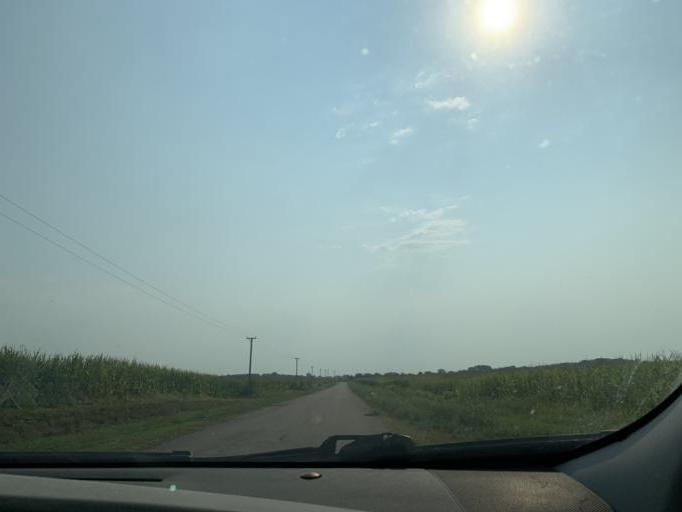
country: US
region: Illinois
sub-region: Whiteside County
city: Morrison
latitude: 41.8698
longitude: -89.9010
